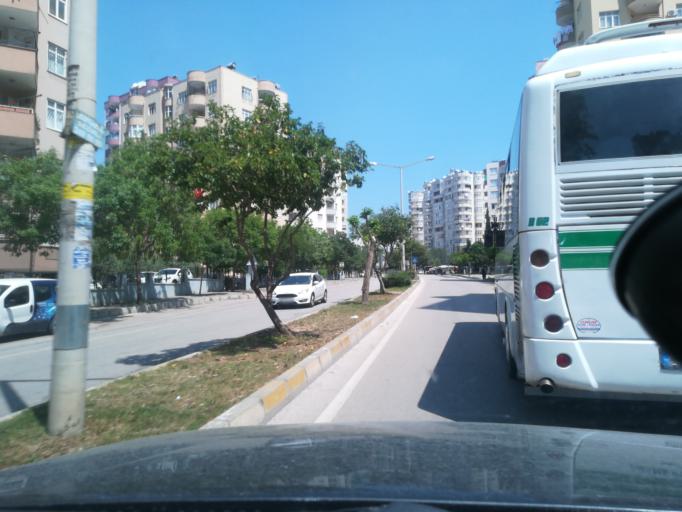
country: TR
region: Adana
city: Seyhan
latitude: 37.0358
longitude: 35.2611
